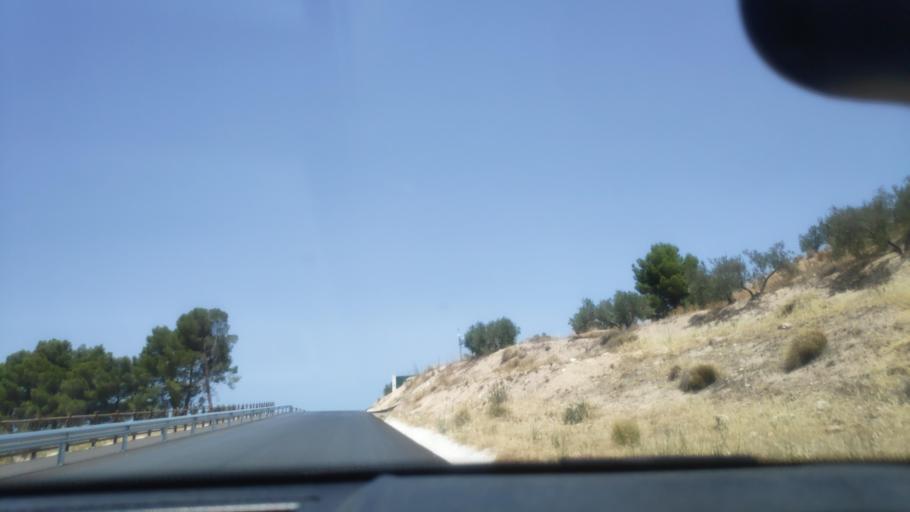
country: ES
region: Andalusia
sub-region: Provincia de Jaen
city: Jodar
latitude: 37.8130
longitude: -3.4131
